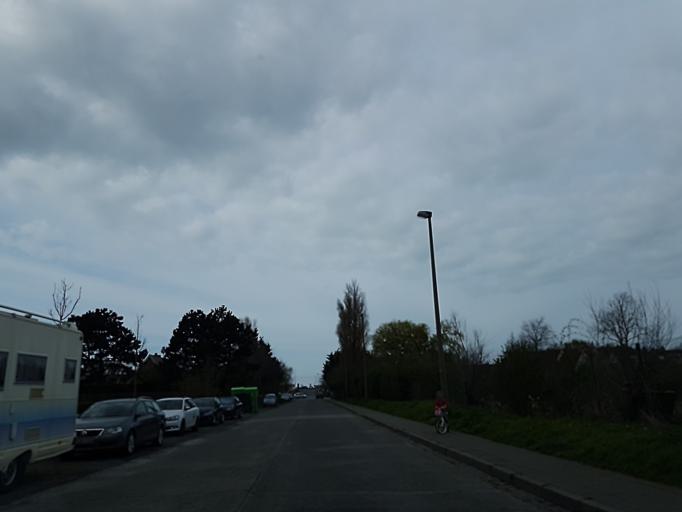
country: BE
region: Flanders
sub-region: Provincie West-Vlaanderen
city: Bredene
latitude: 51.2533
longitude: 2.9856
